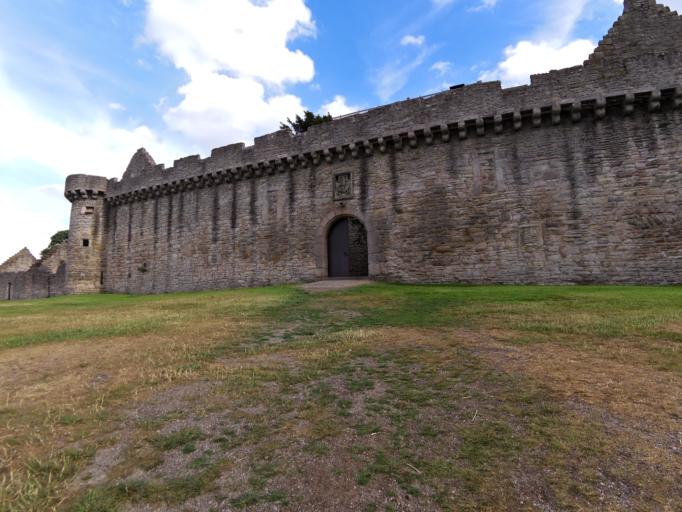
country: GB
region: Scotland
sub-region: West Lothian
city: Seafield
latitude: 55.9259
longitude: -3.1411
